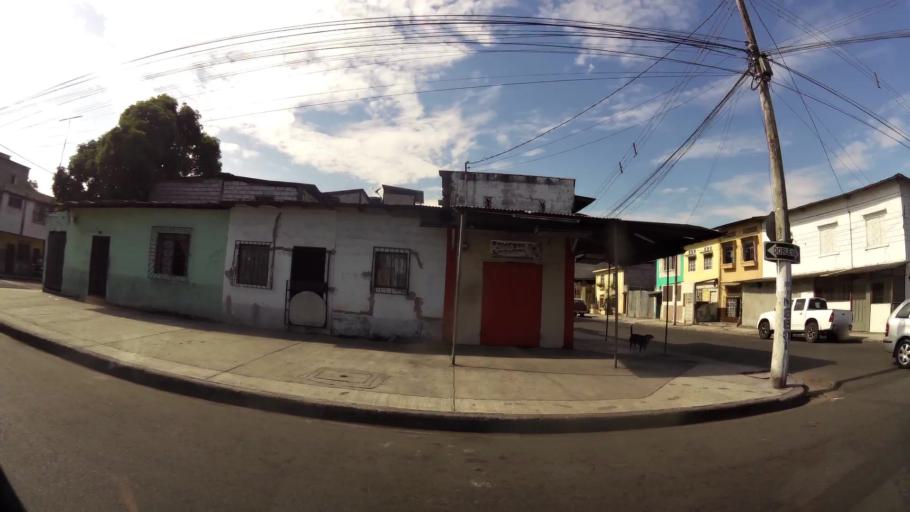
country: EC
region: Guayas
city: Guayaquil
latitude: -2.2154
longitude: -79.9065
